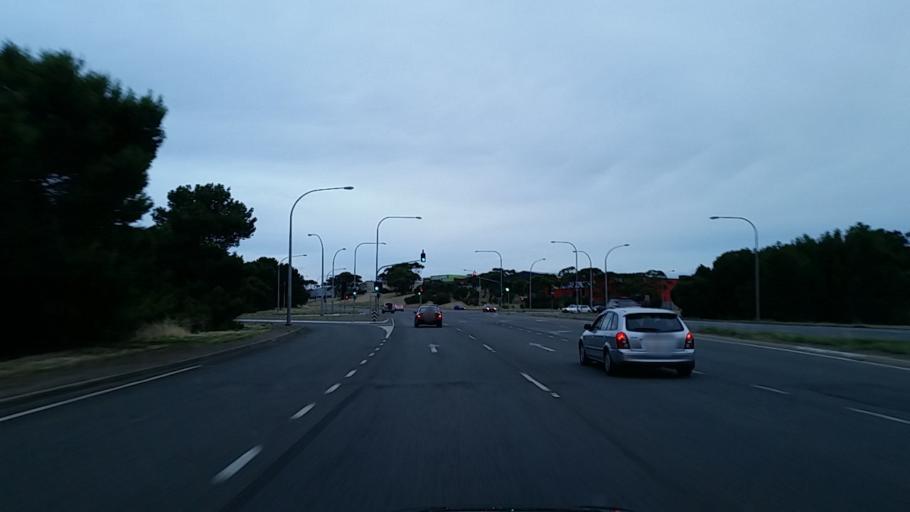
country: AU
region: South Australia
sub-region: Onkaparinga
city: Morphett Vale
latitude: -35.1074
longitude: 138.4982
